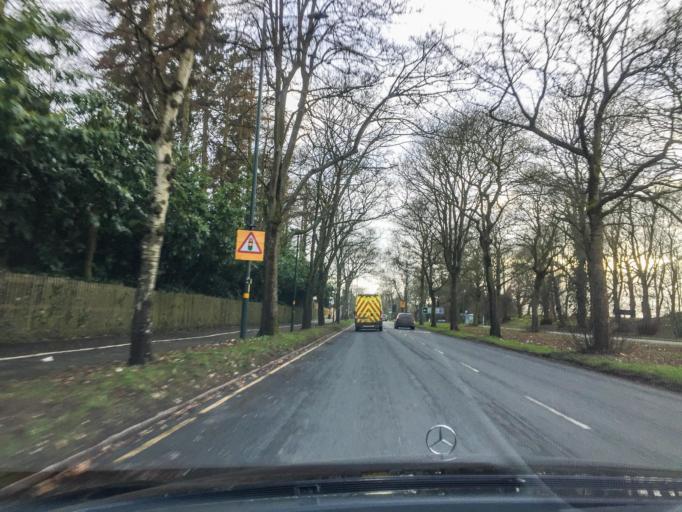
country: GB
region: England
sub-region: City and Borough of Birmingham
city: Bartley Green
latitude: 52.4225
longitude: -1.9593
